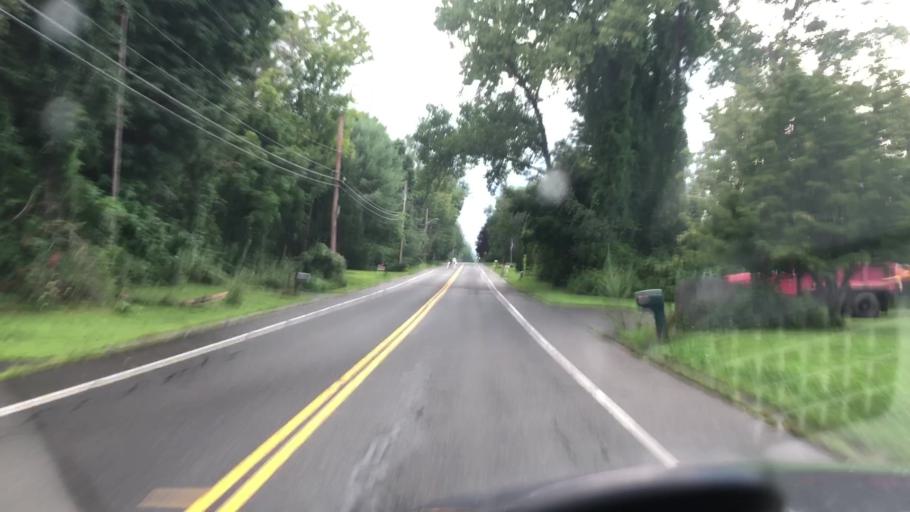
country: US
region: Massachusetts
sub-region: Hampshire County
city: Easthampton
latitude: 42.3026
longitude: -72.6887
